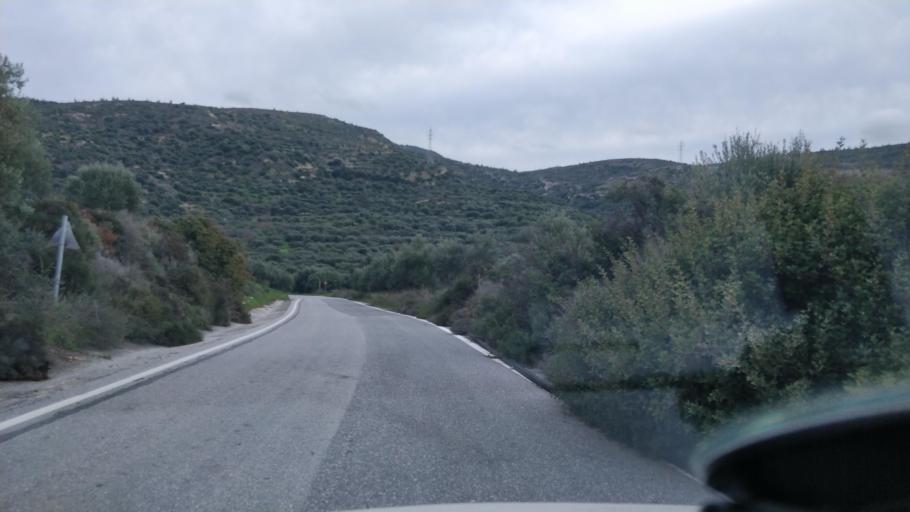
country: GR
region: Crete
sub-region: Nomos Lasithiou
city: Kritsa
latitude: 35.0955
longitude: 25.6956
